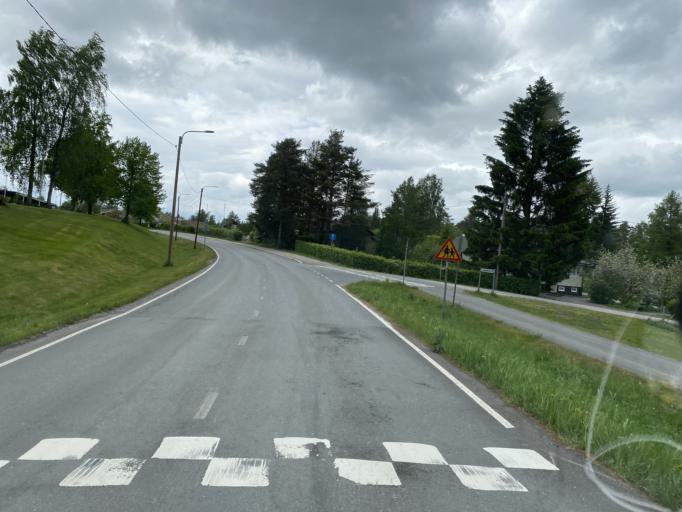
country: FI
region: Pirkanmaa
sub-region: Etelae-Pirkanmaa
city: Urjala
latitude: 61.0796
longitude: 23.5637
